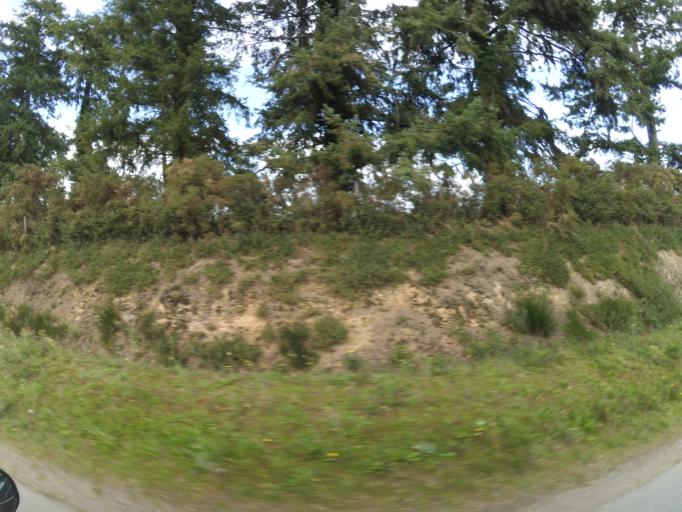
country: FR
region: Brittany
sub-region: Departement du Morbihan
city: Peillac
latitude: 47.7185
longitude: -2.2381
